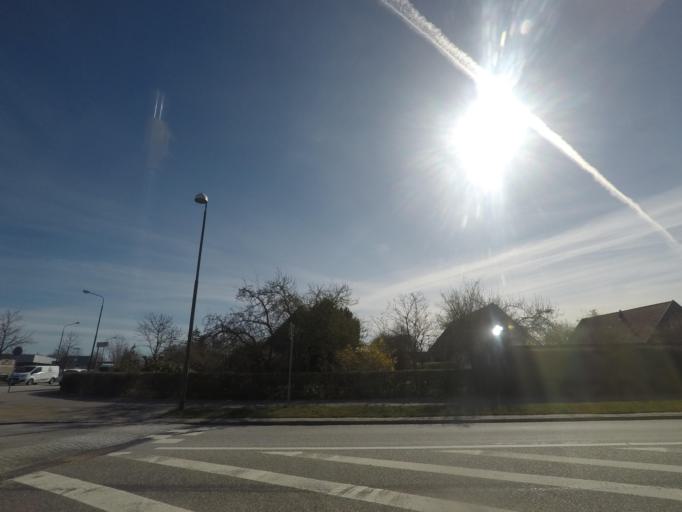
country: SE
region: Skane
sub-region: Burlovs Kommun
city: Arloev
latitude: 55.5780
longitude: 13.0613
